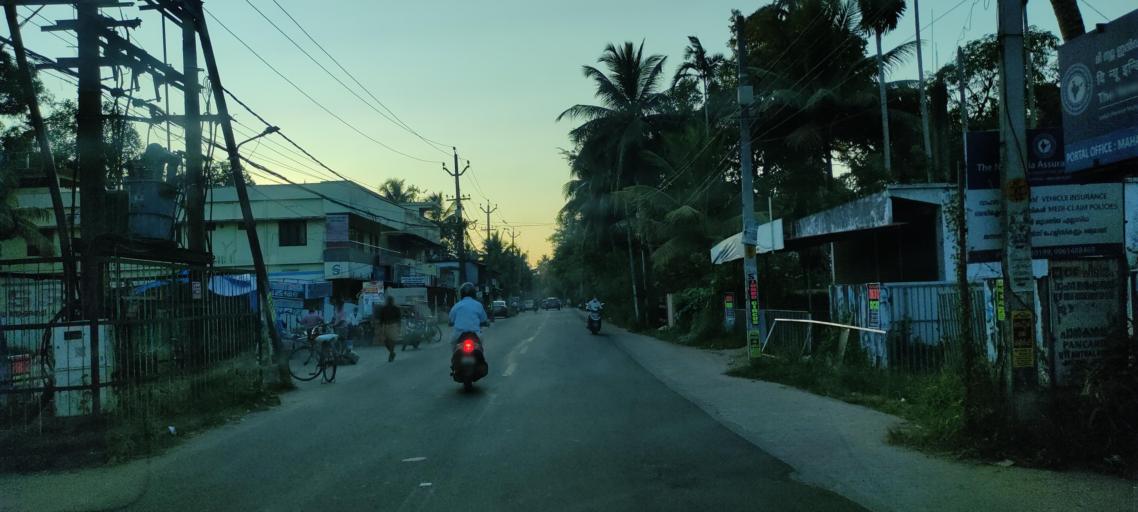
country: IN
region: Kerala
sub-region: Alappuzha
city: Kayankulam
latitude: 9.2592
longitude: 76.4374
